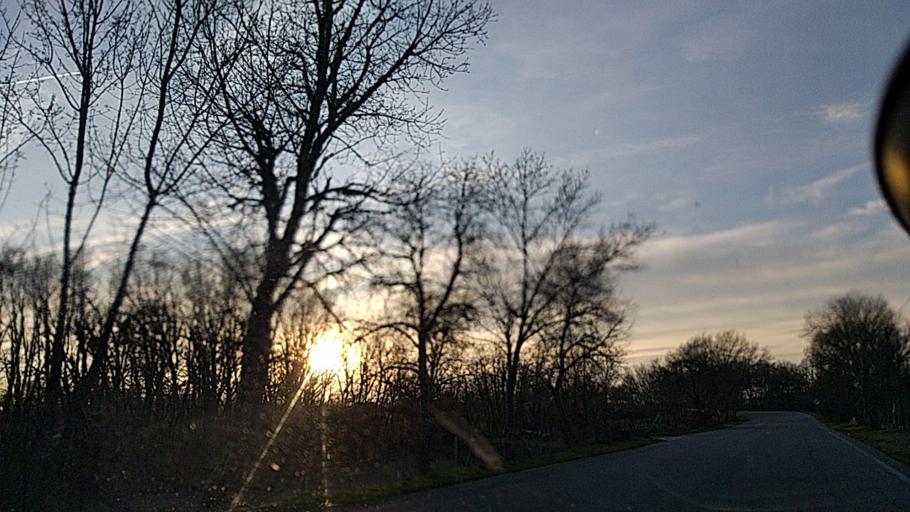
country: PT
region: Guarda
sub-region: Guarda
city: Sequeira
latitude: 40.5998
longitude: -7.0904
